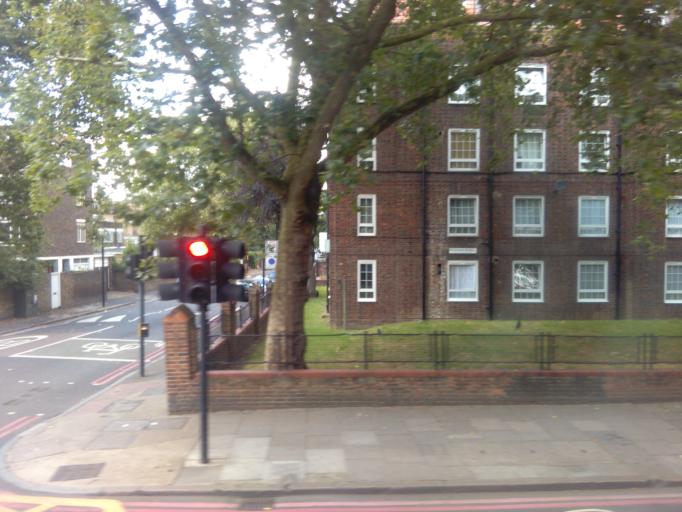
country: GB
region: England
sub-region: Greater London
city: Camberwell
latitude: 51.4737
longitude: -0.0864
